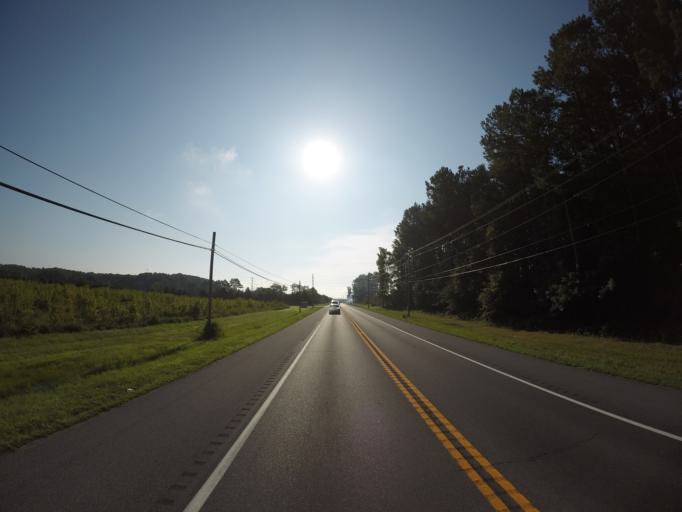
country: US
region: Delaware
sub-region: Sussex County
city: Georgetown
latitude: 38.6983
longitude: -75.4327
